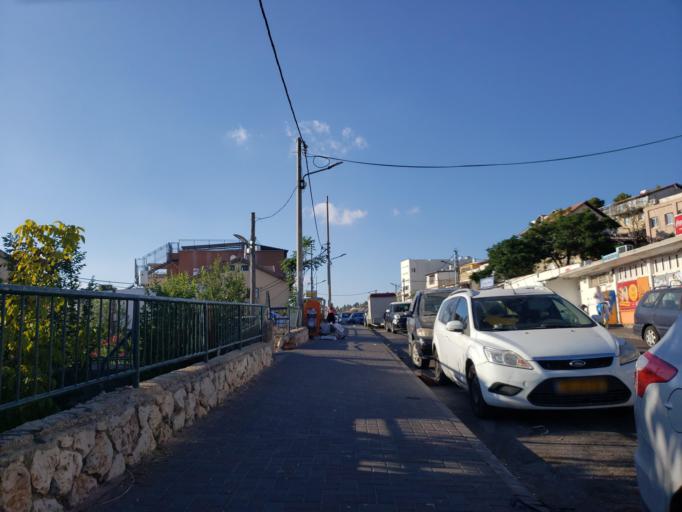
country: IL
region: Northern District
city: Safed
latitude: 32.9585
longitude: 35.4918
